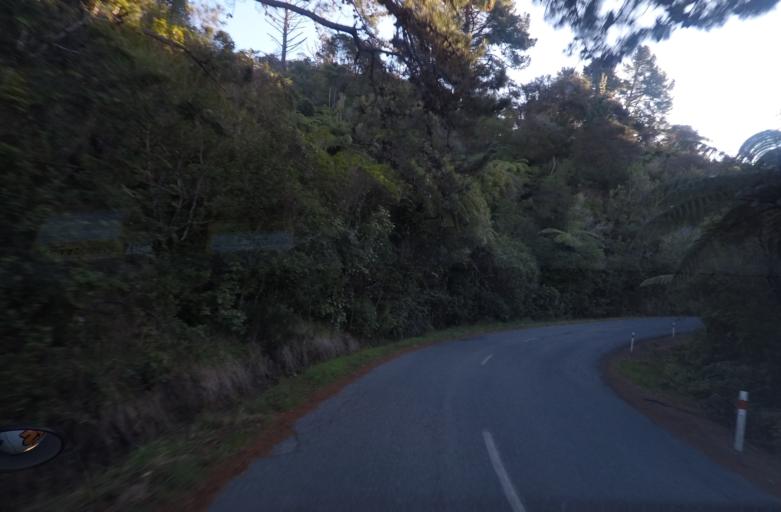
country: NZ
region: Marlborough
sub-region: Marlborough District
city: Picton
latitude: -41.2703
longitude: 173.9485
